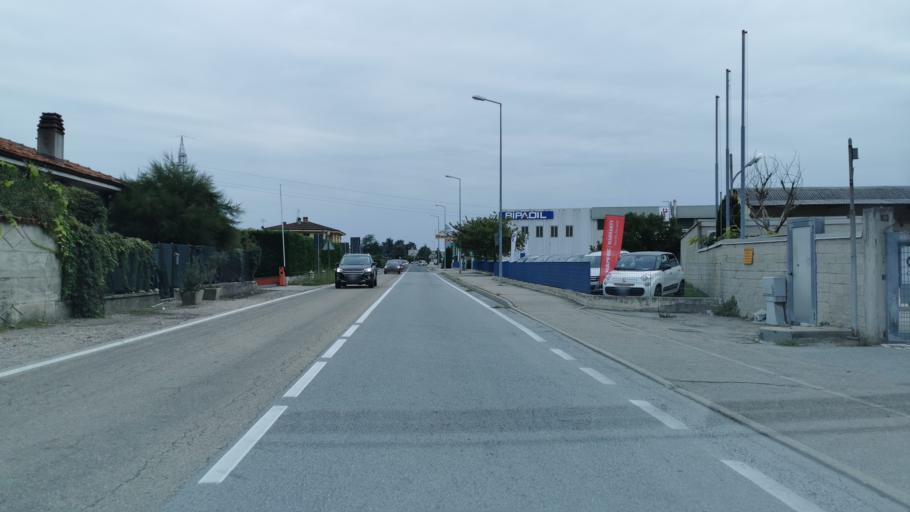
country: IT
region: Piedmont
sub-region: Provincia di Cuneo
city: Roreto
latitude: 44.6800
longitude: 7.8466
